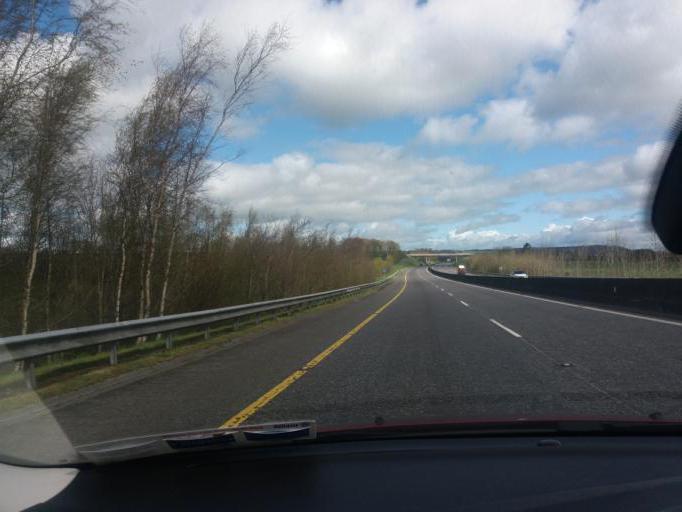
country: IE
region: Munster
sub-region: County Cork
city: Rathcormac
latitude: 52.0621
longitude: -8.3045
